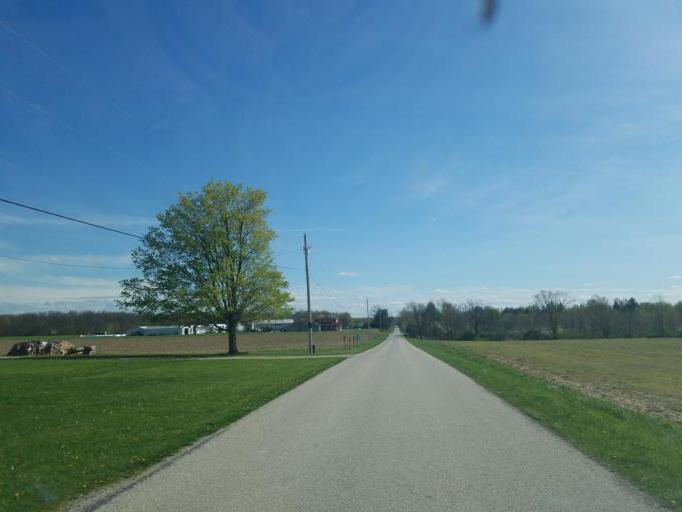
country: US
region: Ohio
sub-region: Huron County
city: Willard
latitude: 41.0820
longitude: -82.7675
